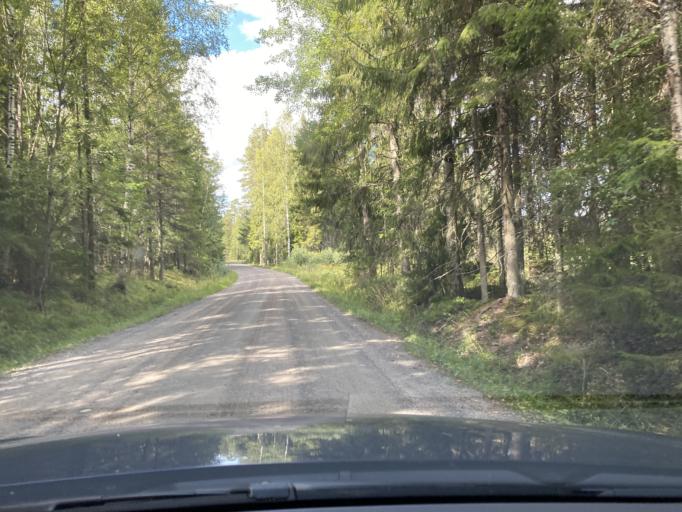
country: FI
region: Haeme
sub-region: Forssa
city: Humppila
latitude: 61.0576
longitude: 23.2641
